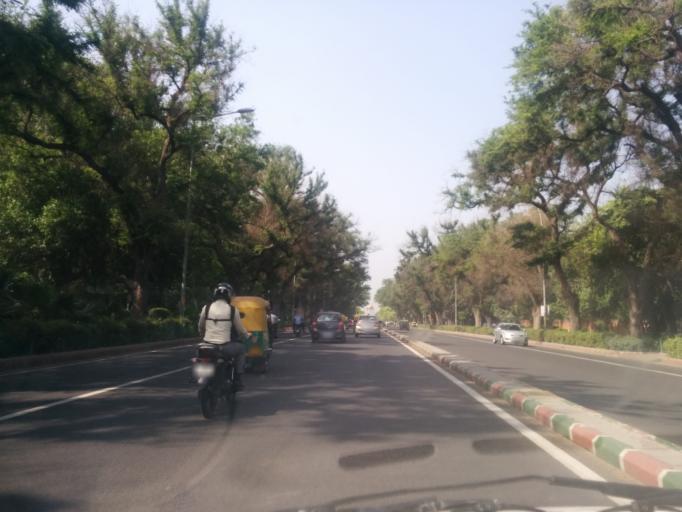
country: IN
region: NCT
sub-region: New Delhi
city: New Delhi
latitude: 28.6180
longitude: 77.2350
